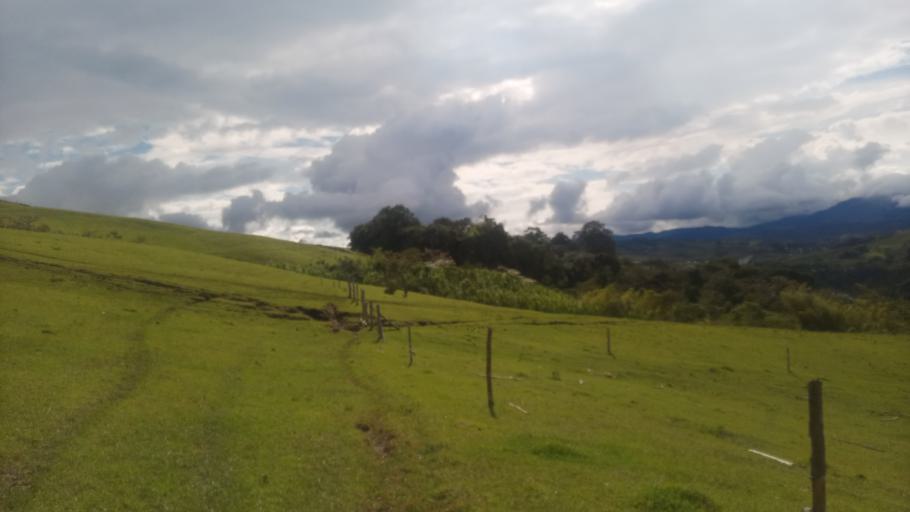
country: CO
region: Valle del Cauca
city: Yotoco
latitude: 3.8846
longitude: -76.4421
